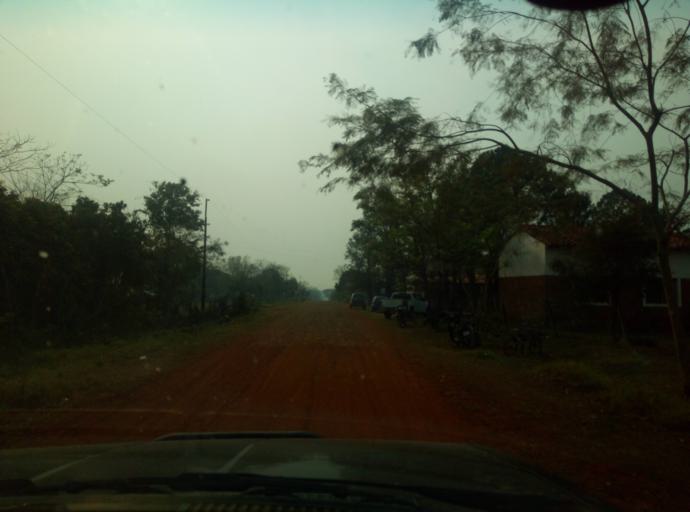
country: PY
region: Caaguazu
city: Carayao
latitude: -25.2041
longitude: -56.2458
